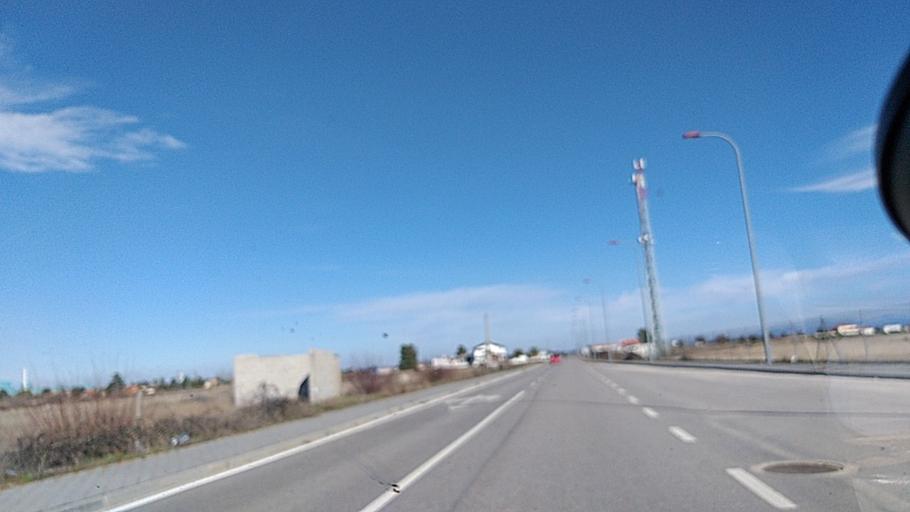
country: ES
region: Castille and Leon
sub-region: Provincia de Salamanca
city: Fuentes de Onoro
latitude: 40.6168
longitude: -6.8534
